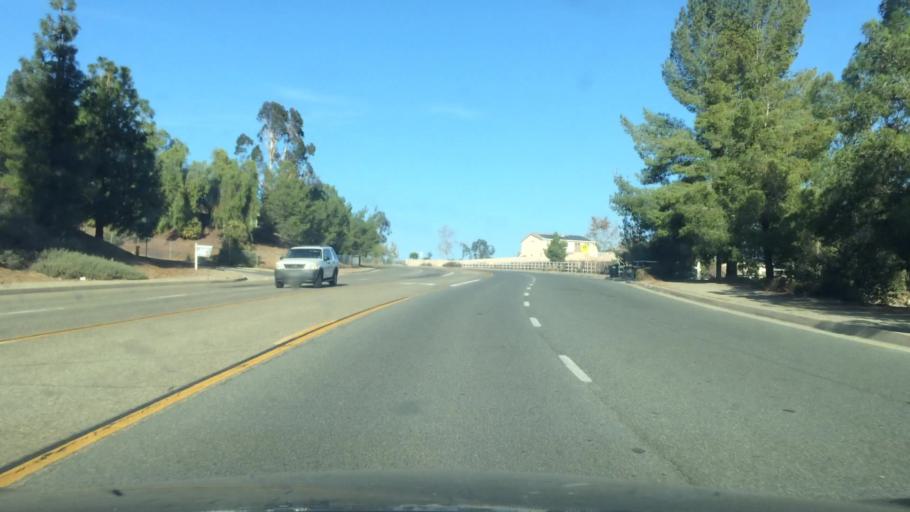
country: US
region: California
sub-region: Riverside County
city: Lakeland Village
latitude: 33.6803
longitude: -117.3980
